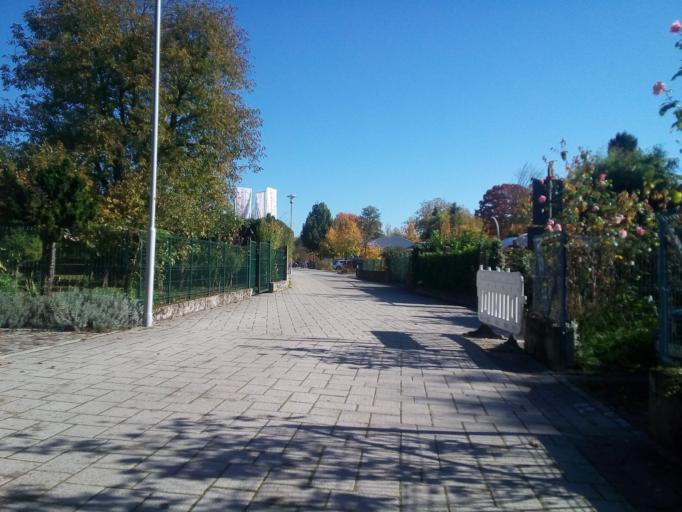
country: DE
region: Baden-Wuerttemberg
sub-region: Karlsruhe Region
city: Lichtenau
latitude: 48.7260
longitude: 8.0066
